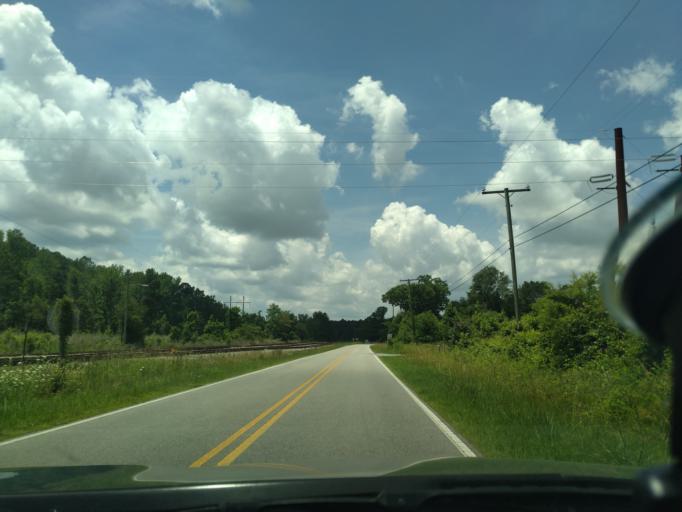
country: US
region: North Carolina
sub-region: Washington County
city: Plymouth
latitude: 35.8507
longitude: -76.7650
